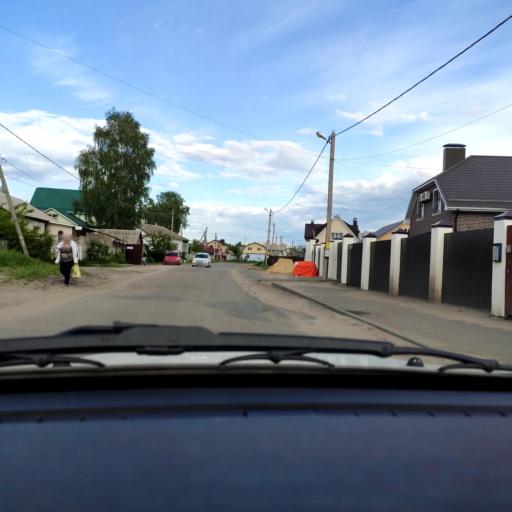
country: RU
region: Voronezj
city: Podgornoye
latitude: 51.7401
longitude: 39.1525
